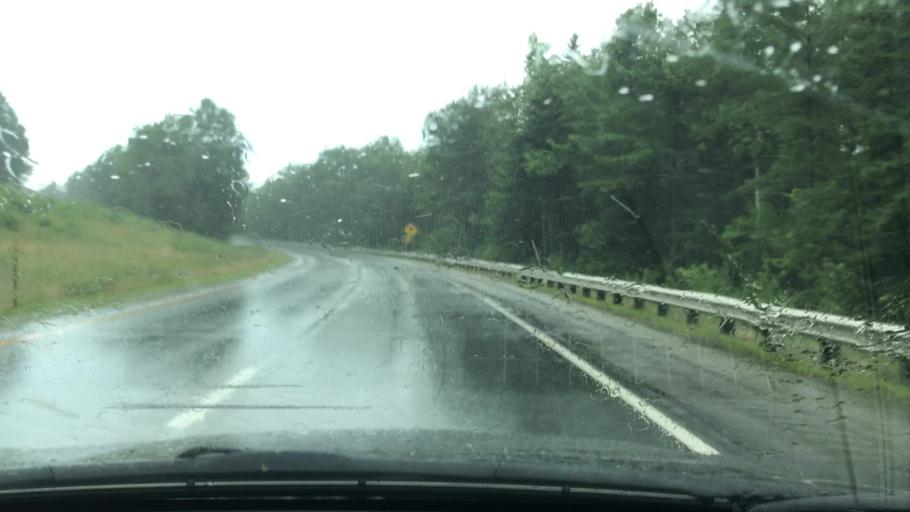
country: US
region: New Hampshire
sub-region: Grafton County
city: Littleton
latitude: 44.2920
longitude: -71.7512
